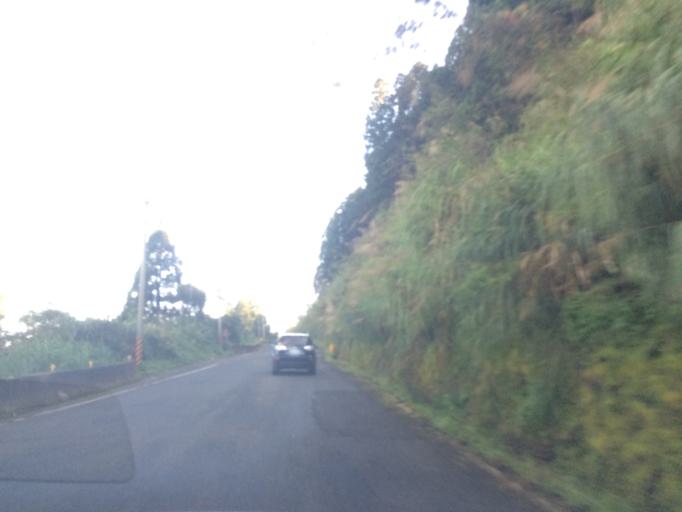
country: TW
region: Taiwan
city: Lugu
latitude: 23.6607
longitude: 120.7752
